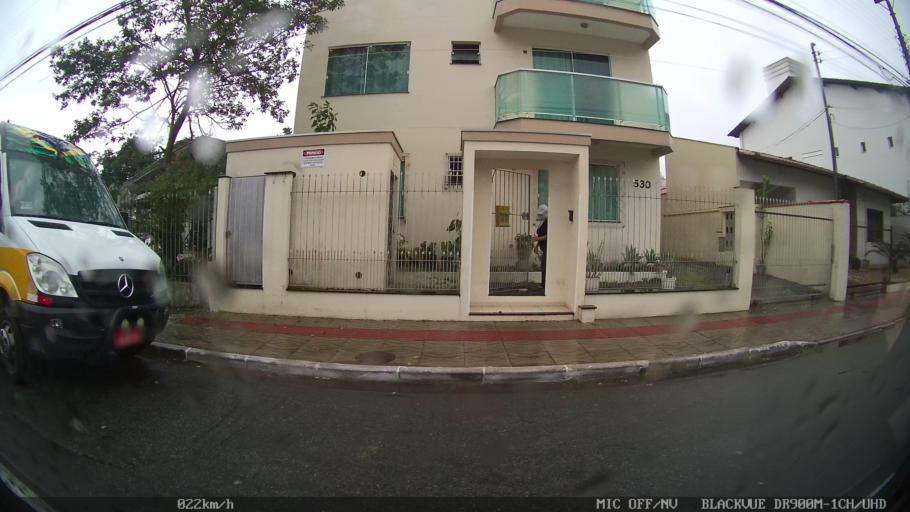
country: BR
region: Santa Catarina
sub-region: Itajai
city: Itajai
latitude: -26.9153
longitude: -48.6664
